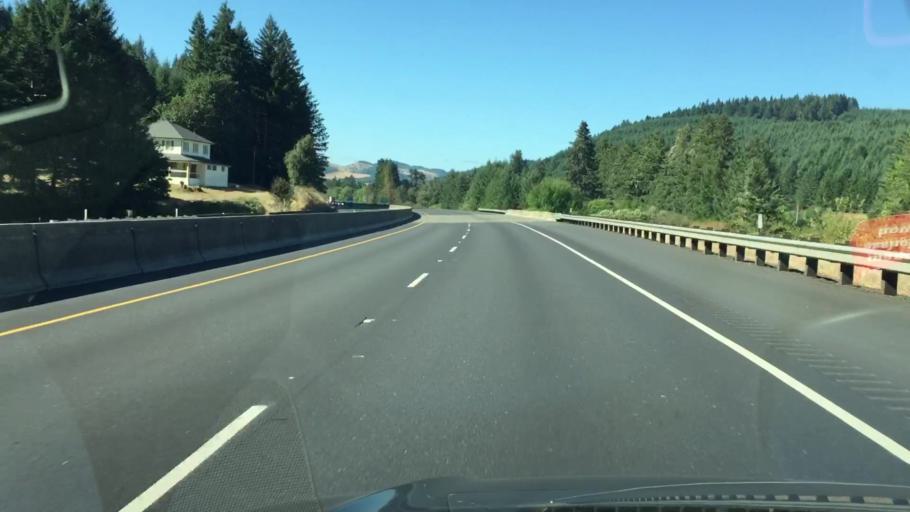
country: US
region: Oregon
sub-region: Lane County
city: Cottage Grove
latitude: 43.7366
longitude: -123.1924
